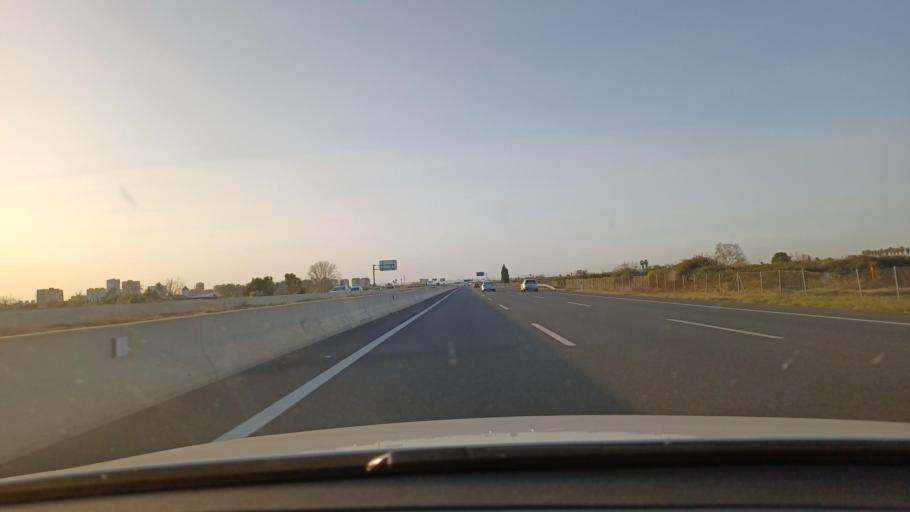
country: ES
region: Valencia
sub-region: Provincia de Valencia
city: Puig
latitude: 39.5794
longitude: -0.2946
